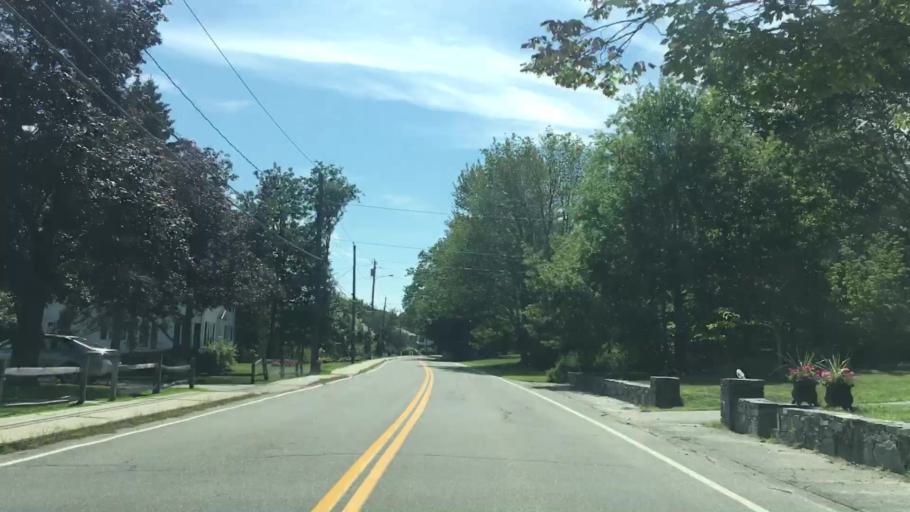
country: US
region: Maine
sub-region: Cumberland County
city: South Portland
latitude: 43.6223
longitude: -70.2536
